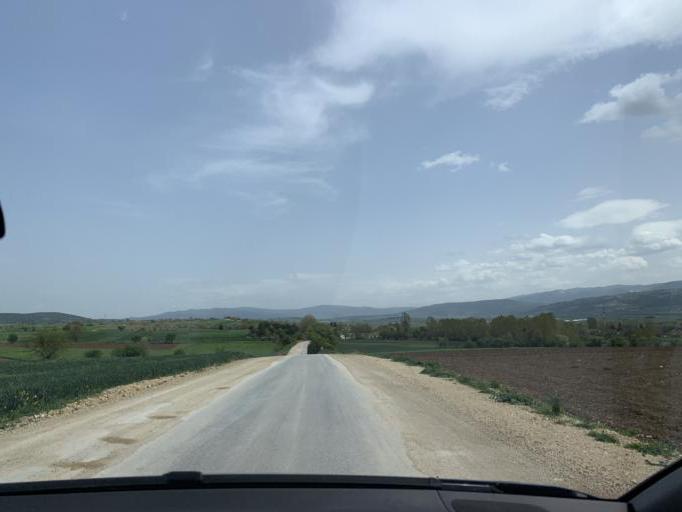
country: TR
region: Bolu
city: Bolu
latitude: 40.7588
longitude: 31.6858
